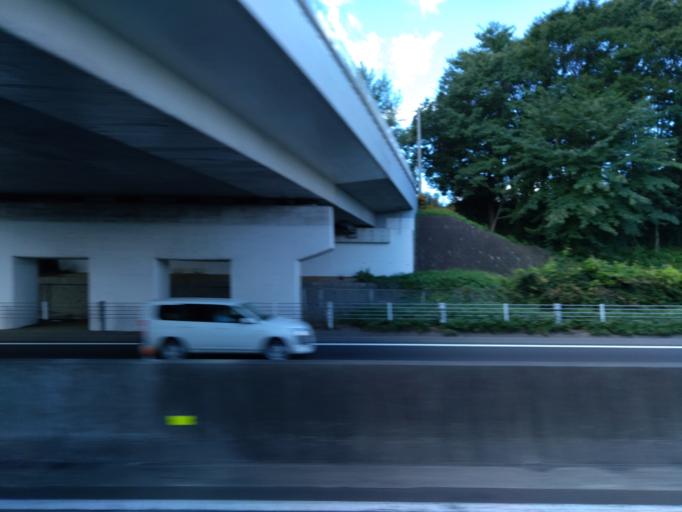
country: JP
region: Miyagi
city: Tomiya
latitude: 38.3347
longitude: 140.8555
